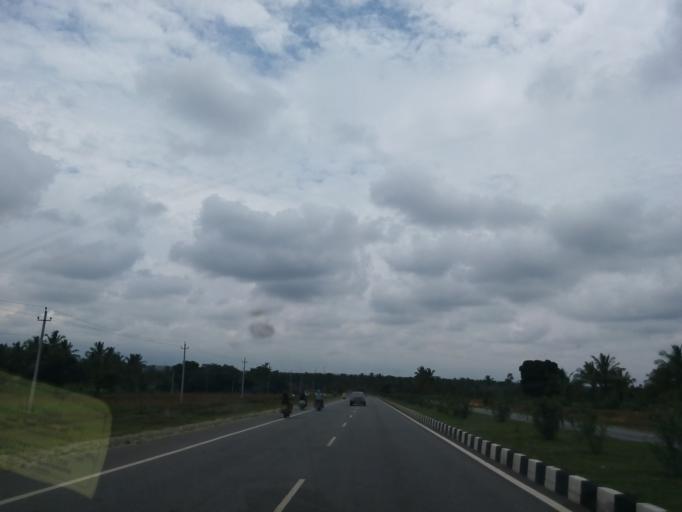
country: IN
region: Karnataka
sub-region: Hassan
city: Channarayapatna
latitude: 12.9771
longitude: 76.2526
